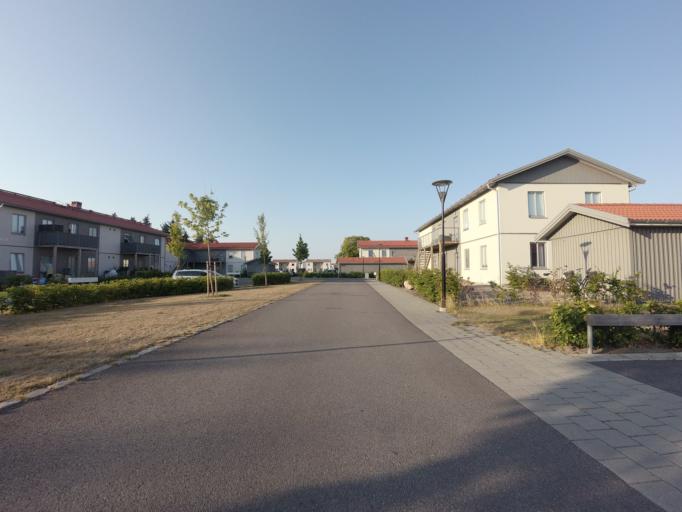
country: SE
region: Skane
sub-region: Hoganas Kommun
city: Hoganas
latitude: 56.1552
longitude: 12.5843
